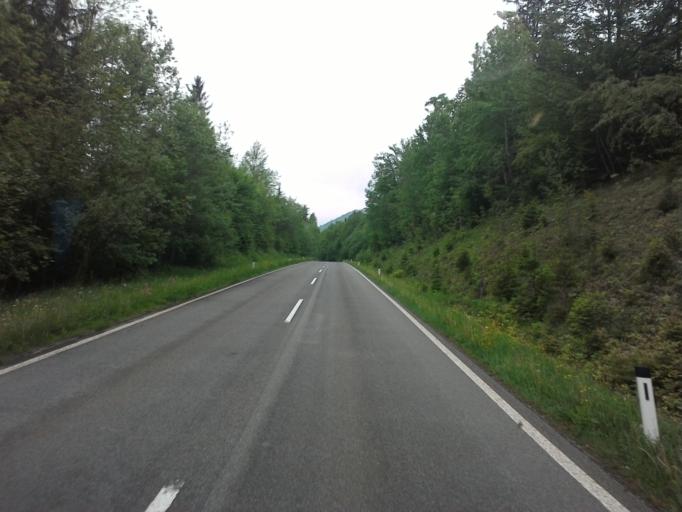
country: AT
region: Styria
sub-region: Politischer Bezirk Liezen
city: Altenmarkt bei Sankt Gallen
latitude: 47.7089
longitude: 14.6846
